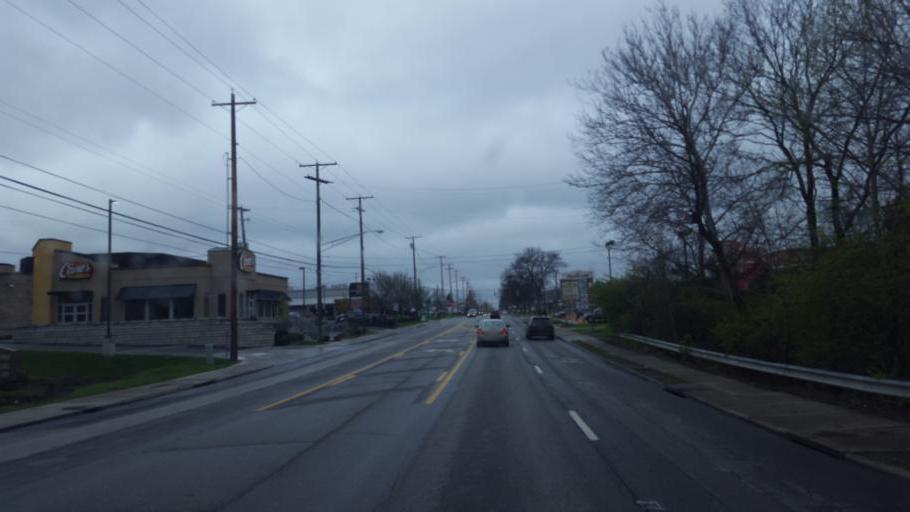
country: US
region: Ohio
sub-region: Franklin County
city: Worthington
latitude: 40.0672
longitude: -83.0193
